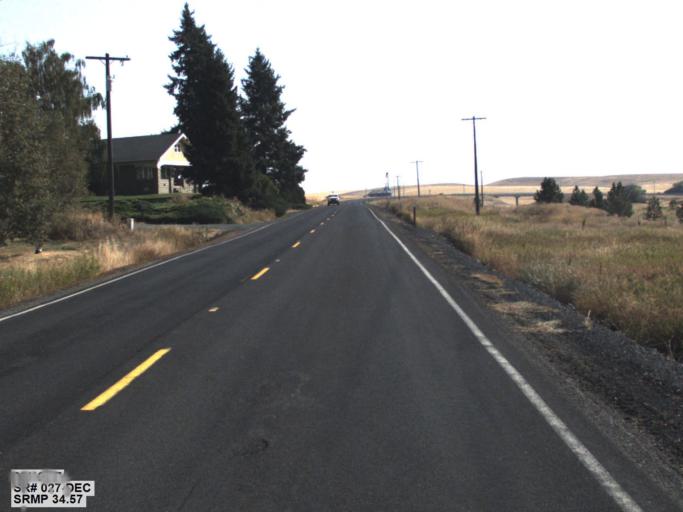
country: US
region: Washington
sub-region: Whitman County
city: Colfax
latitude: 47.1244
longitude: -117.2094
